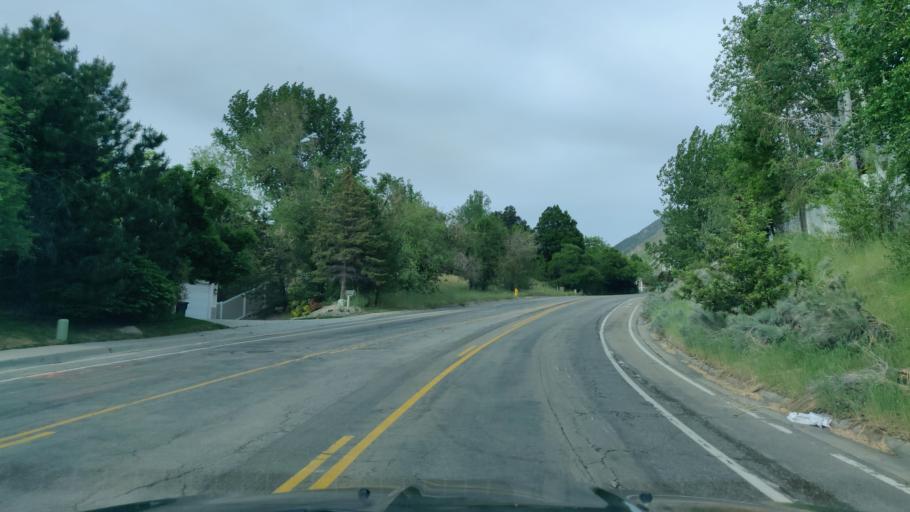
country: US
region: Utah
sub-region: Salt Lake County
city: Cottonwood Heights
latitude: 40.6041
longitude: -111.8132
